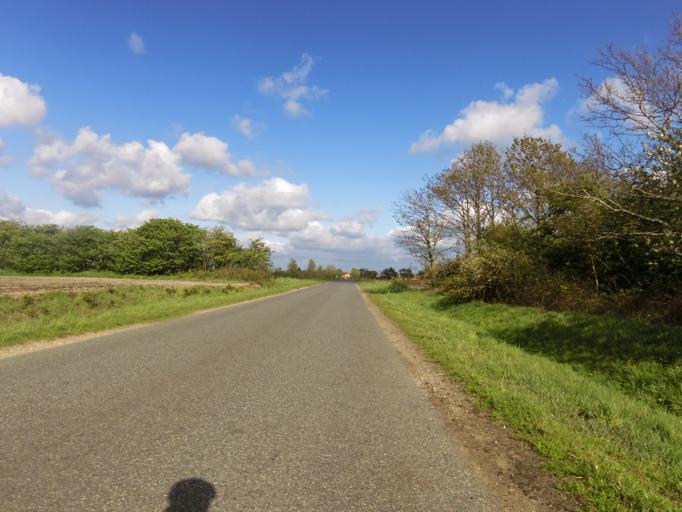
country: DK
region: South Denmark
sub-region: Esbjerg Kommune
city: Ribe
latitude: 55.2584
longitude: 8.7993
